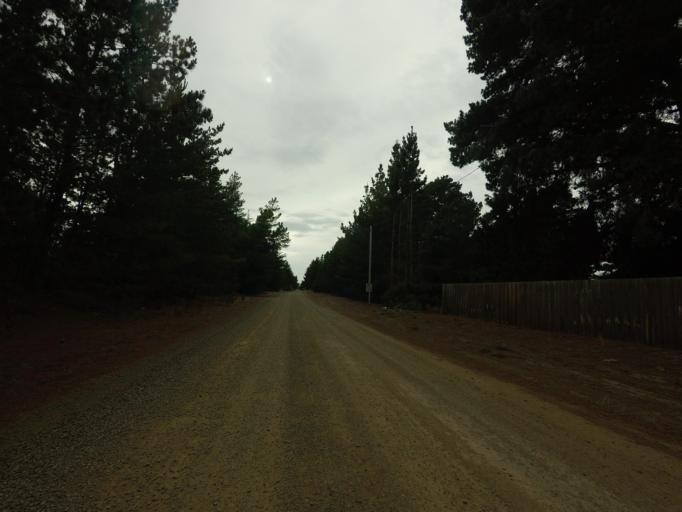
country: AU
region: Tasmania
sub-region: Clarence
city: Seven Mile Beach
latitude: -42.8340
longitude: 147.5371
